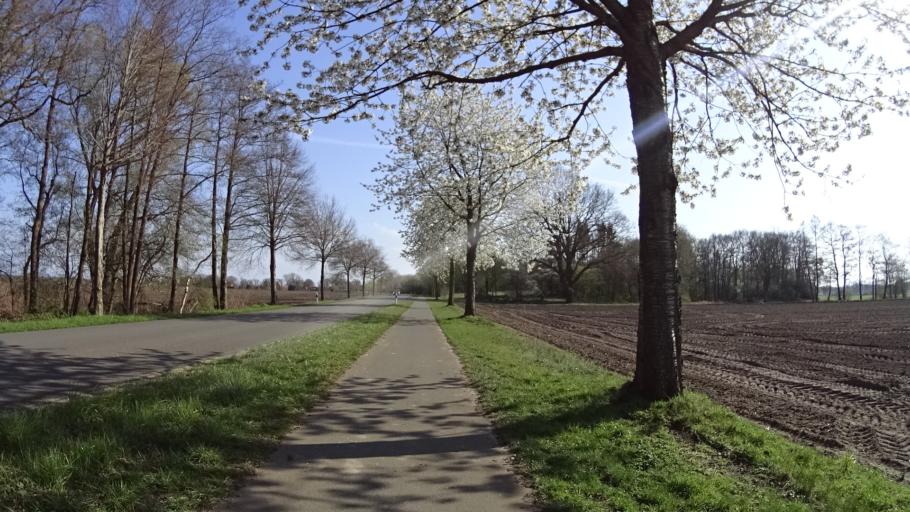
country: DE
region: Lower Saxony
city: Dorpen
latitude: 52.9454
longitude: 7.3159
